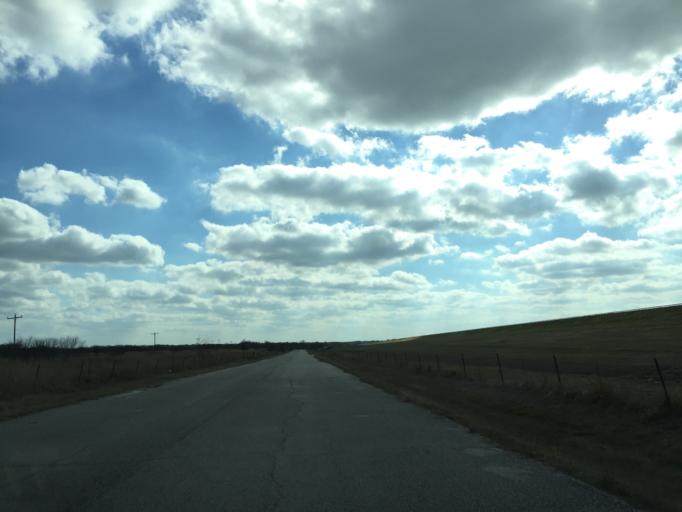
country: US
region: Texas
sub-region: Williamson County
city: Granger
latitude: 30.7117
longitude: -97.3232
